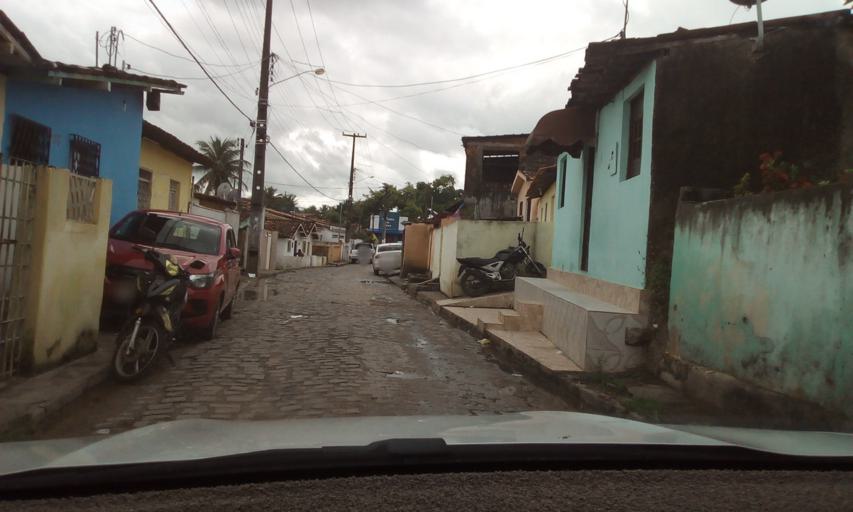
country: BR
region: Paraiba
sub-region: Joao Pessoa
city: Joao Pessoa
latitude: -7.1263
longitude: -34.8921
